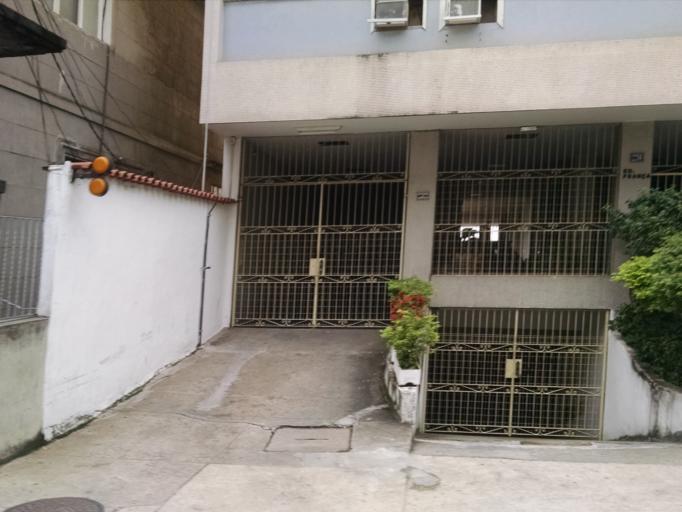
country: BR
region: Rio de Janeiro
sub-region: Rio De Janeiro
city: Rio de Janeiro
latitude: -22.9293
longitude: -43.1949
